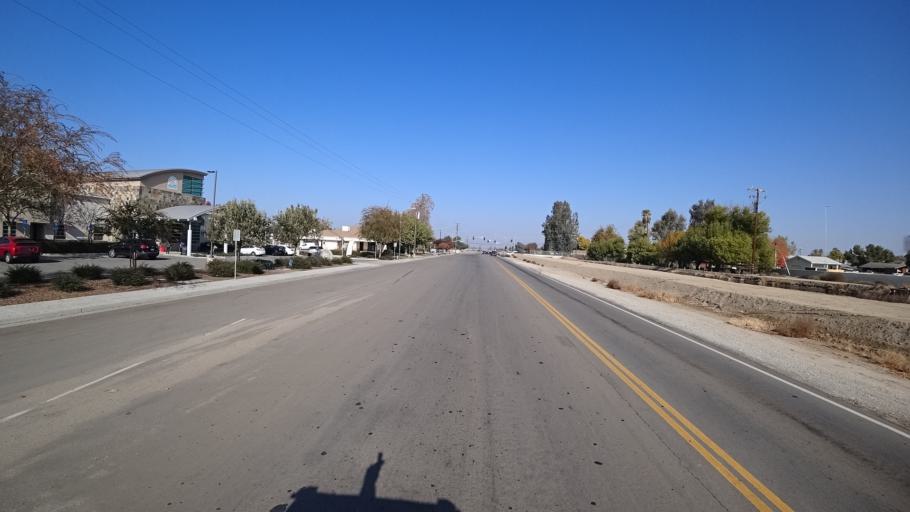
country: US
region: California
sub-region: Kern County
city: Greenfield
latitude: 35.2726
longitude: -119.0213
